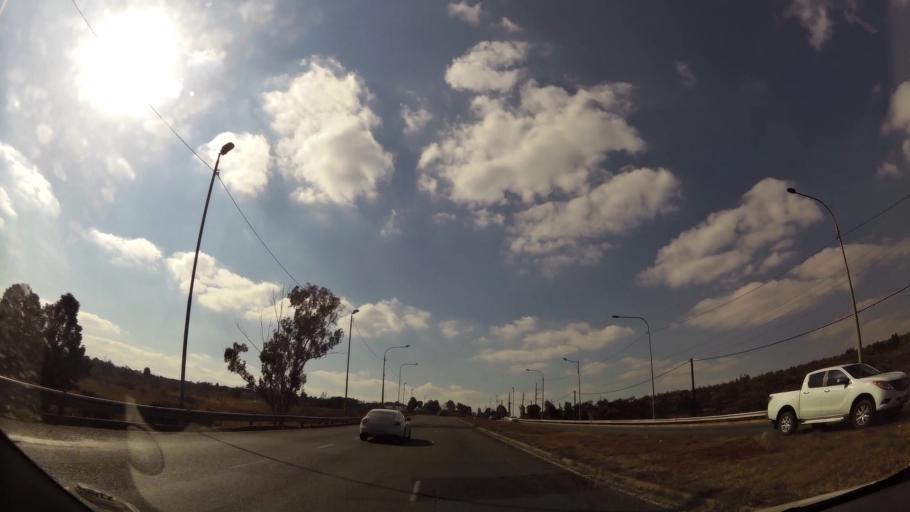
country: ZA
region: Gauteng
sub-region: West Rand District Municipality
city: Krugersdorp
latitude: -26.0661
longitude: 27.8048
